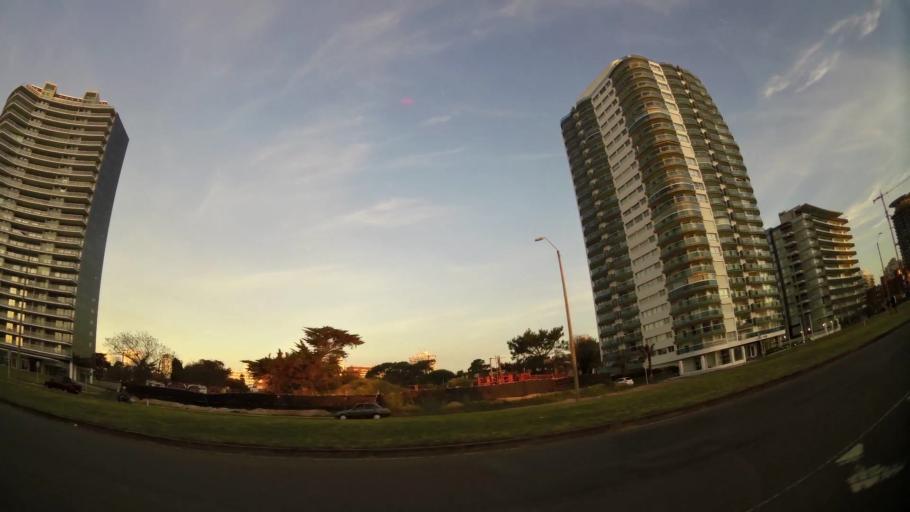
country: UY
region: Maldonado
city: Punta del Este
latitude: -34.9488
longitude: -54.9374
